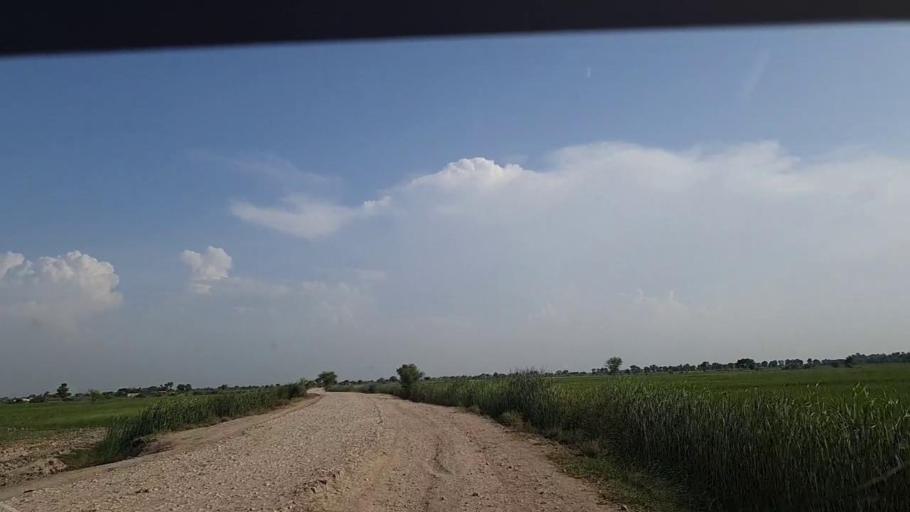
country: PK
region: Sindh
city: Khanpur
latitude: 27.8540
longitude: 69.3771
